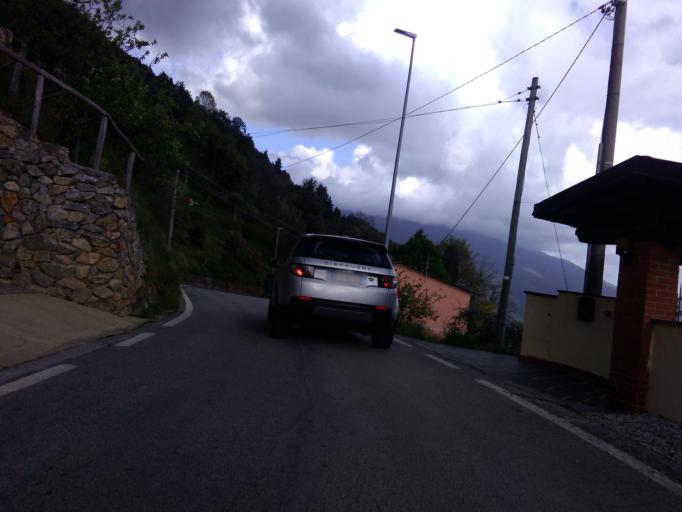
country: IT
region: Tuscany
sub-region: Provincia di Lucca
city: Pontestazzemese
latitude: 43.9572
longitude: 10.2792
